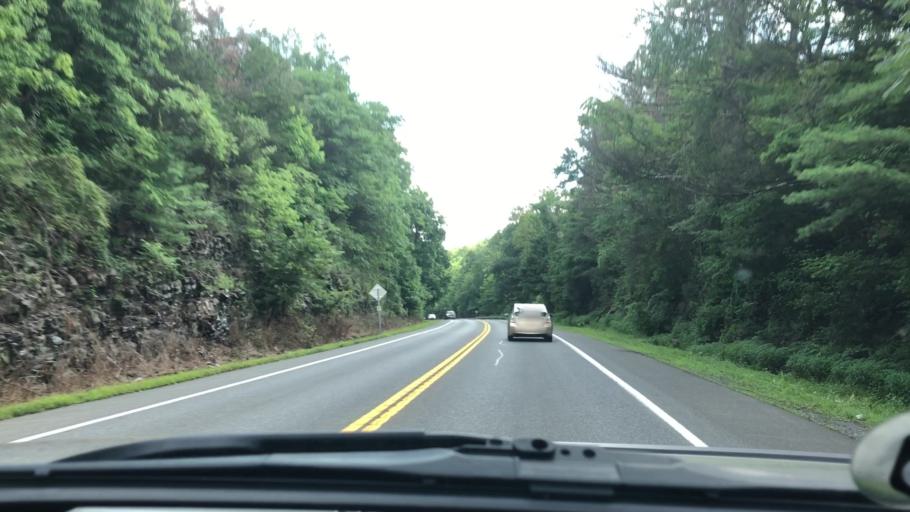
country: US
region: New York
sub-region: Ulster County
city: Manorville
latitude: 42.1191
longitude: -73.9887
